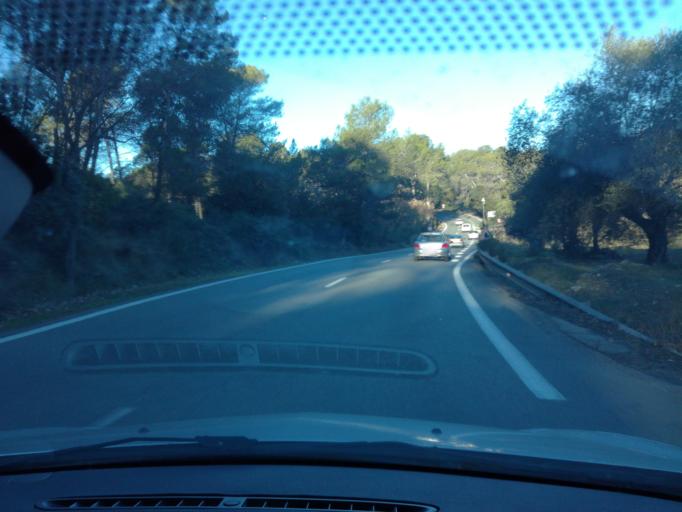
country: FR
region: Provence-Alpes-Cote d'Azur
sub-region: Departement des Alpes-Maritimes
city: Vallauris
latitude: 43.6097
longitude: 7.0517
